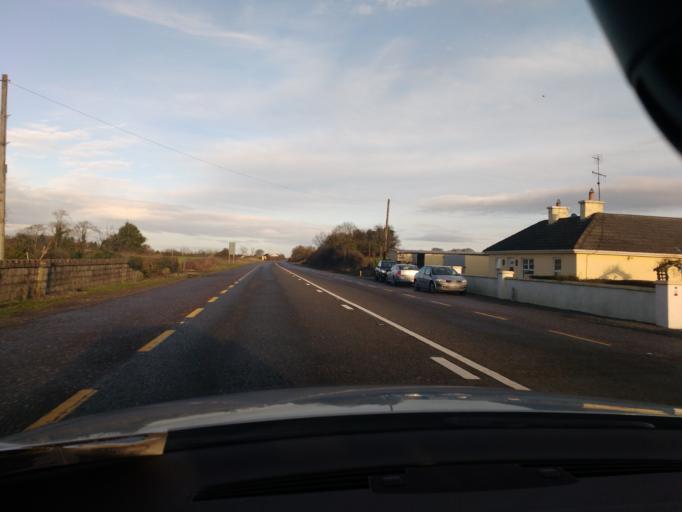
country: IE
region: Munster
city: Thurles
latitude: 52.6505
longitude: -7.7173
